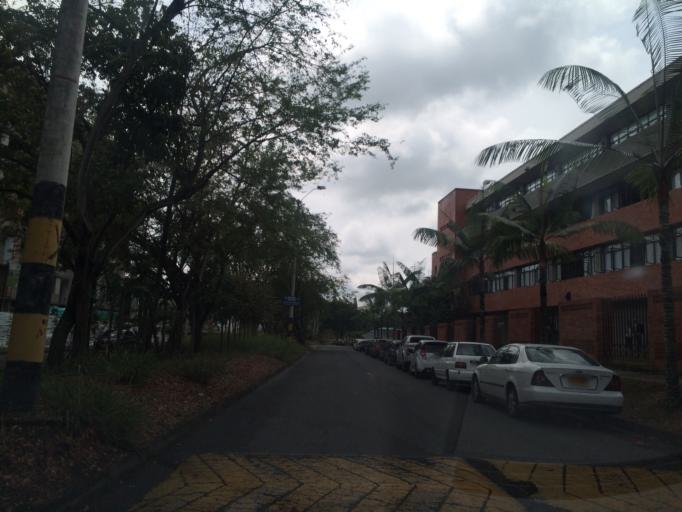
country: CO
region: Valle del Cauca
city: Cali
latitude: 3.3544
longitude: -76.5214
